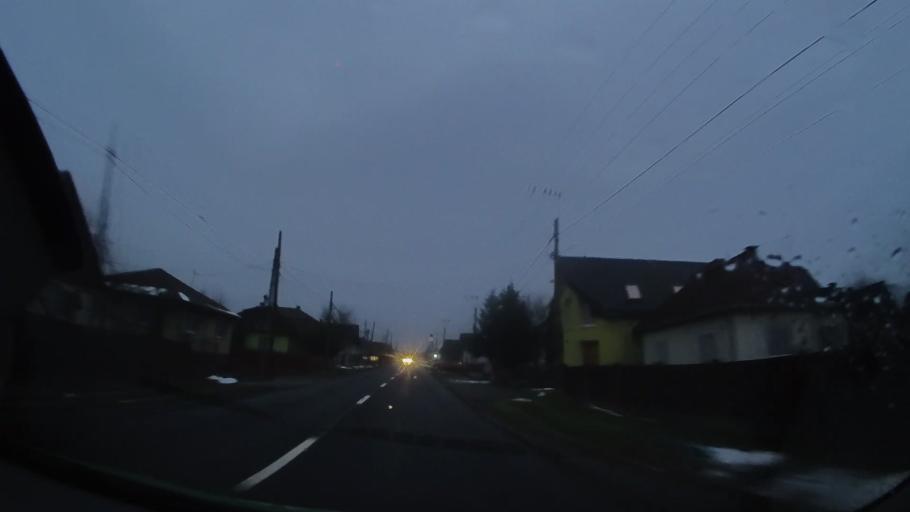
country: RO
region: Harghita
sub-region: Comuna Remetea
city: Remetea
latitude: 46.8000
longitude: 25.4661
